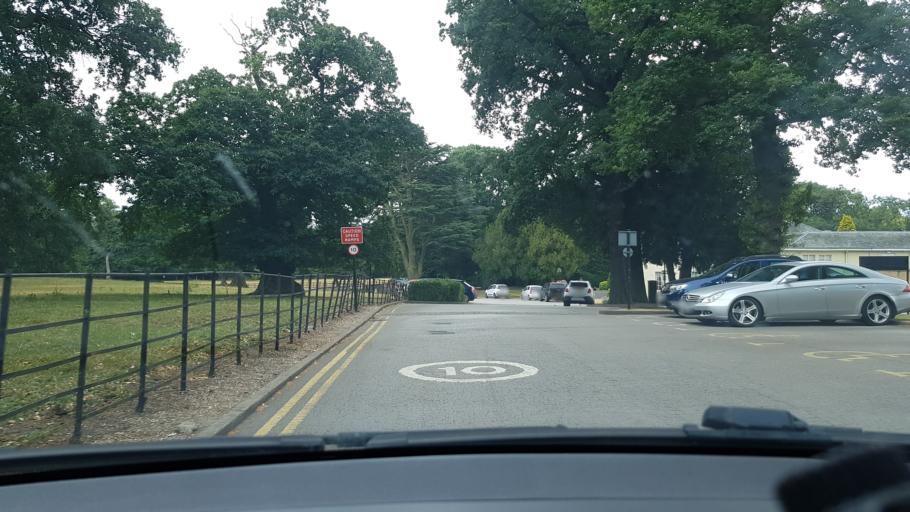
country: GB
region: England
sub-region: Nottinghamshire
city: Eastwood
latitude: 53.0248
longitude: -1.3094
